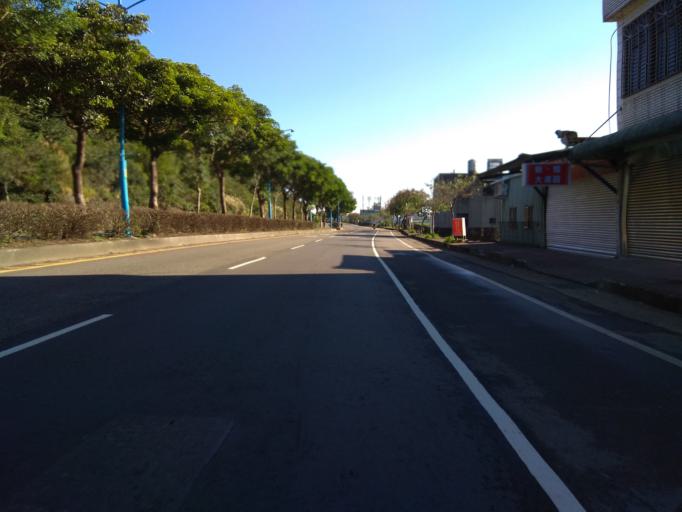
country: TW
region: Taiwan
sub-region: Hsinchu
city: Zhubei
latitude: 24.8968
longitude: 121.1134
